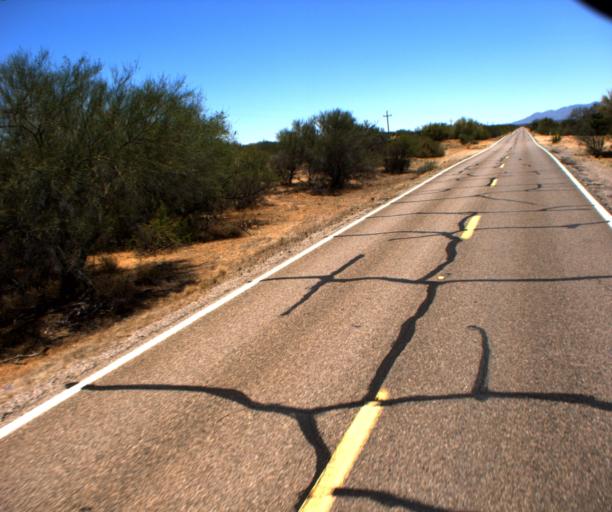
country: US
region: Arizona
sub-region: Pima County
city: Three Points
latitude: 31.9944
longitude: -111.3661
